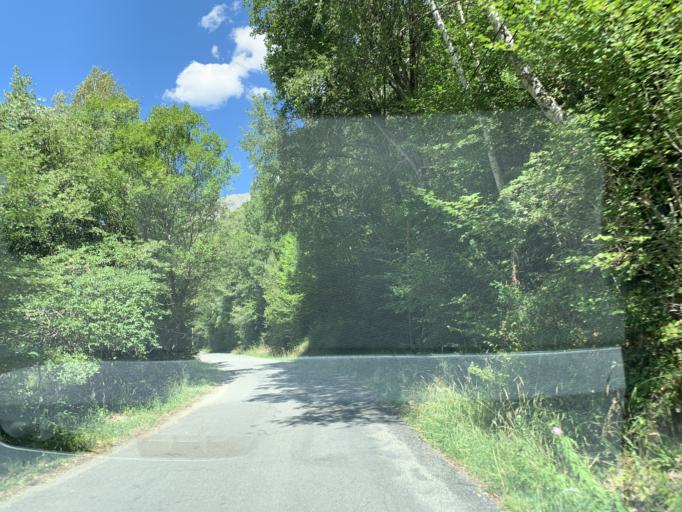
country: ES
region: Aragon
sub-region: Provincia de Huesca
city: Hoz de Jaca
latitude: 42.7112
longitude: -0.3024
